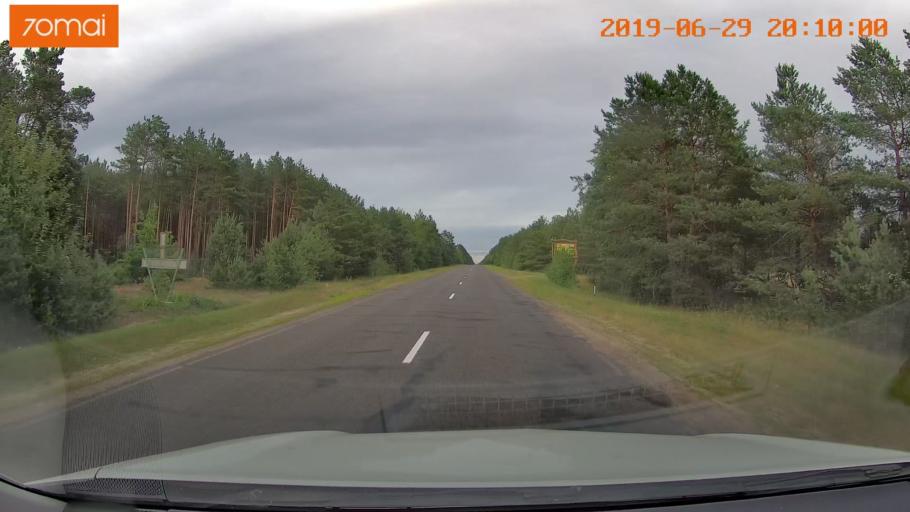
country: BY
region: Brest
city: Lahishyn
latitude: 52.3512
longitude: 26.0834
